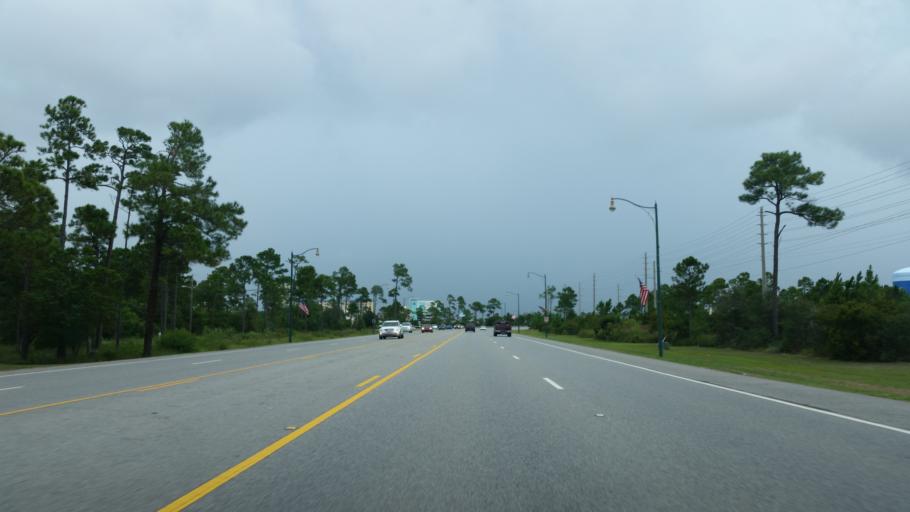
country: US
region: Alabama
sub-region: Baldwin County
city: Orange Beach
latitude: 30.2784
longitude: -87.5809
